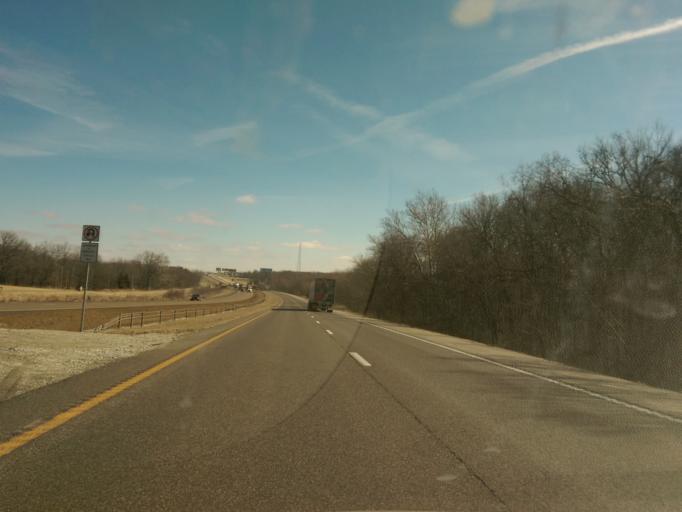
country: US
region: Missouri
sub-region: Boone County
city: Hallsville
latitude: 38.9552
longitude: -92.1577
